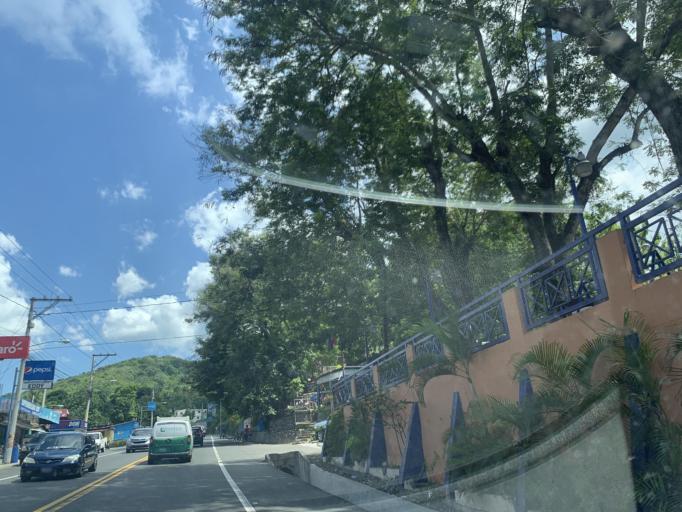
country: DO
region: Puerto Plata
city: Altamira
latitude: 19.6753
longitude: -70.8355
